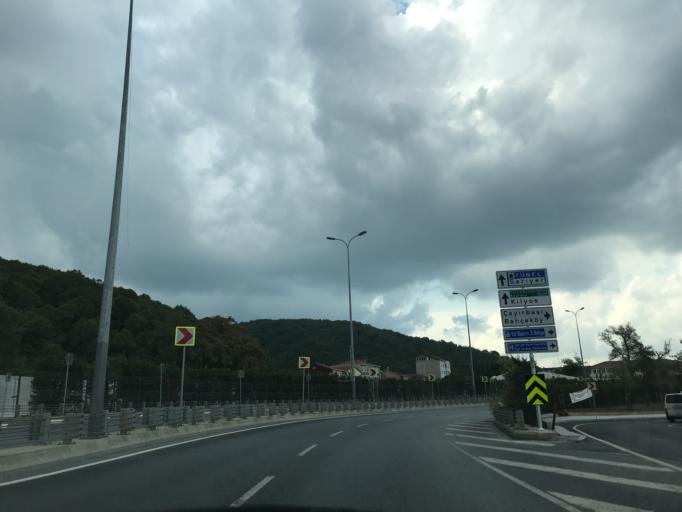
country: TR
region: Istanbul
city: Arikoey
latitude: 41.1535
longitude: 29.0266
